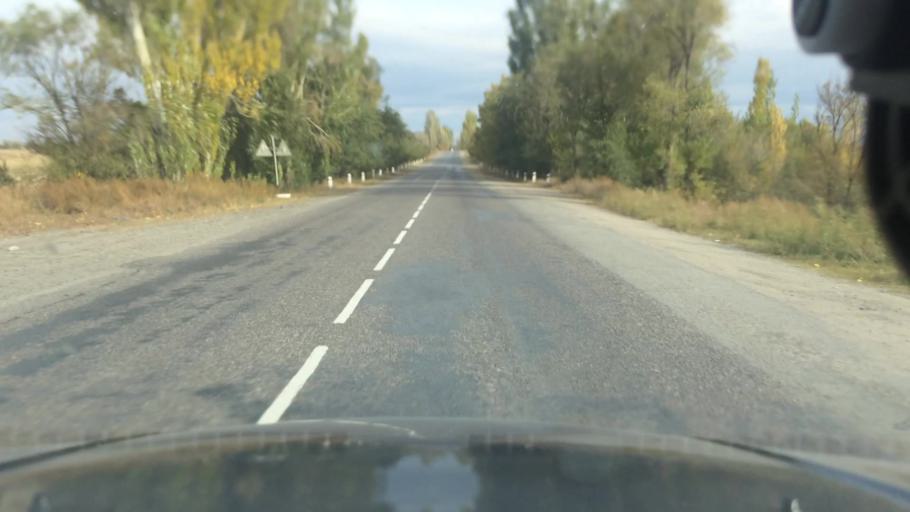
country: KG
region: Ysyk-Koel
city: Karakol
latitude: 42.5655
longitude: 78.3913
